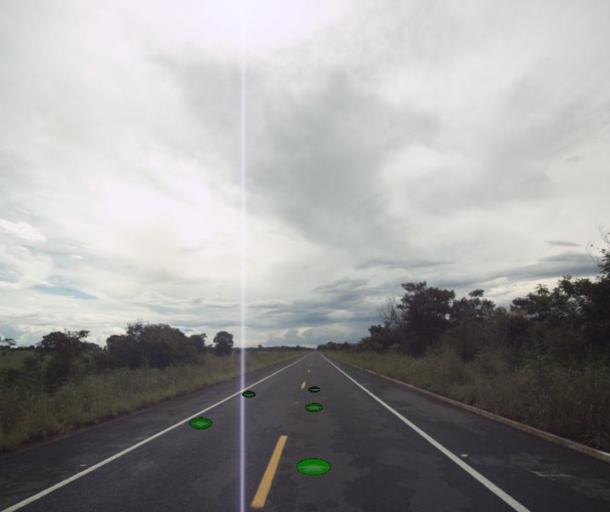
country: BR
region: Goias
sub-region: Sao Miguel Do Araguaia
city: Sao Miguel do Araguaia
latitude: -13.2675
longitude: -50.5101
